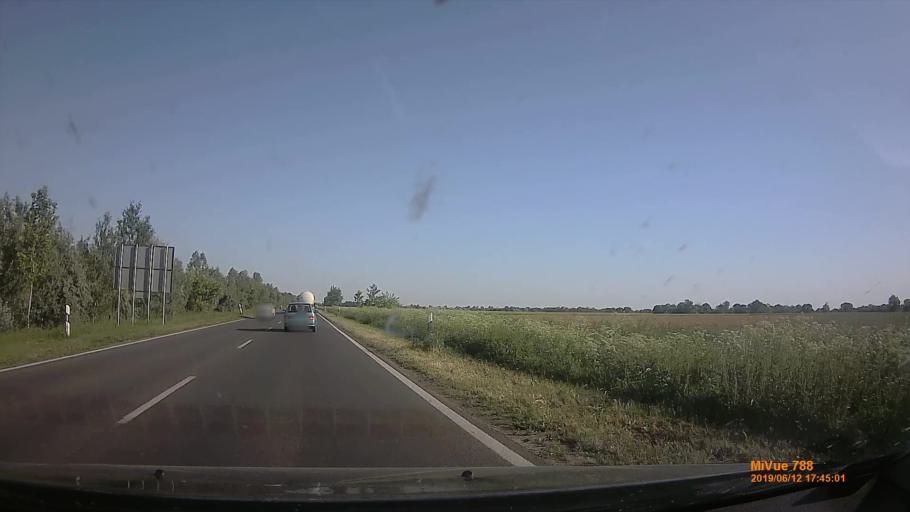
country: HU
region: Csongrad
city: Szeged
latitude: 46.2487
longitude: 20.0828
